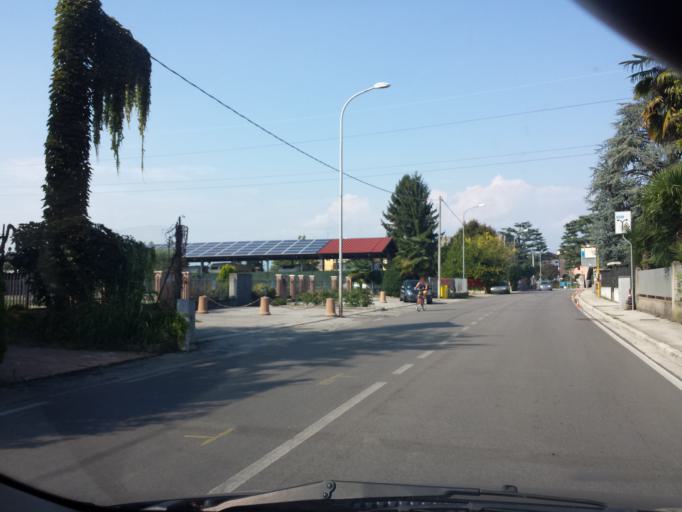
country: IT
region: Veneto
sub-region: Provincia di Vicenza
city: Monticello Conte Otto
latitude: 45.6083
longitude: 11.5693
